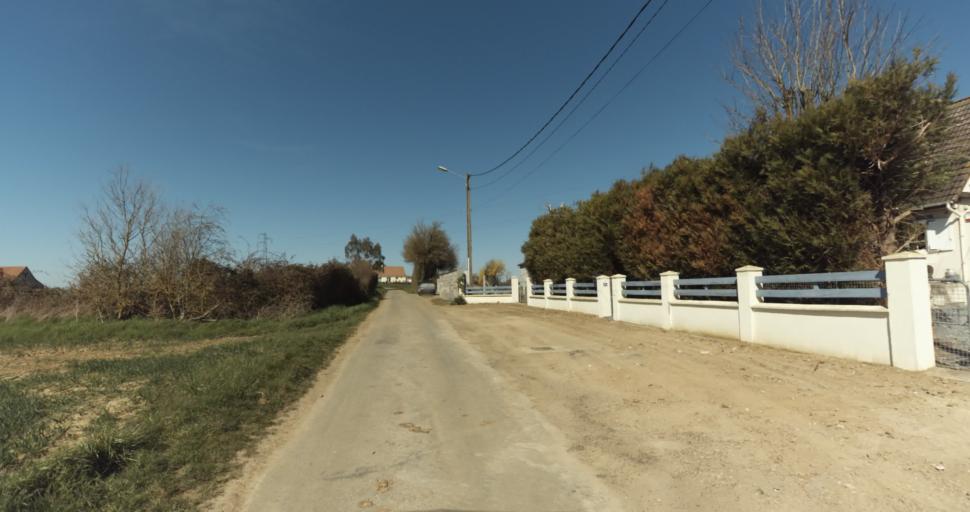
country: FR
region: Lower Normandy
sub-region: Departement du Calvados
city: Saint-Pierre-sur-Dives
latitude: 49.0563
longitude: -0.0143
